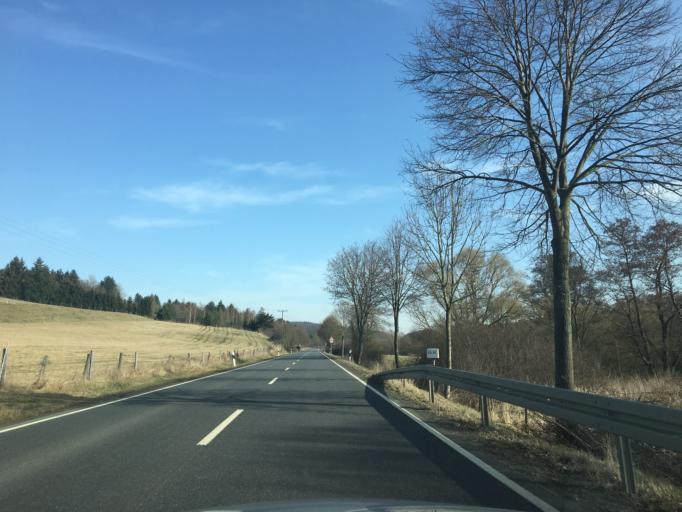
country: DE
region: Hesse
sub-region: Regierungsbezirk Giessen
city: Schwalmtal
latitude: 50.6690
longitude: 9.2752
